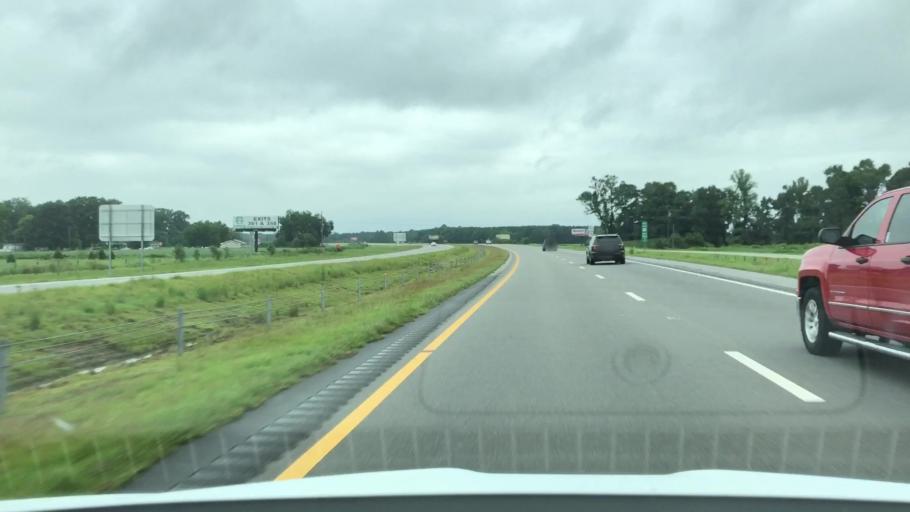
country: US
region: North Carolina
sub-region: Wayne County
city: Elroy
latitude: 35.3879
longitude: -77.8654
